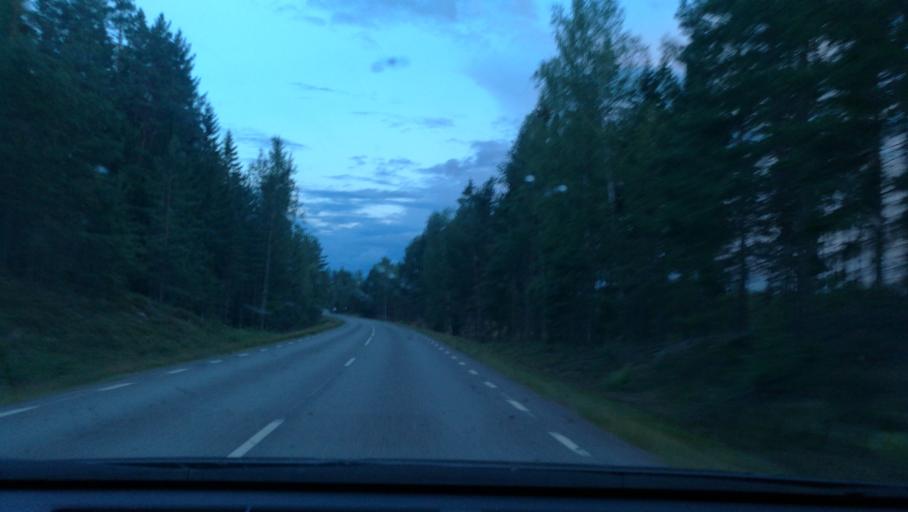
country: SE
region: OEstergoetland
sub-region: Norrkopings Kommun
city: Svartinge
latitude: 58.8104
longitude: 15.9405
